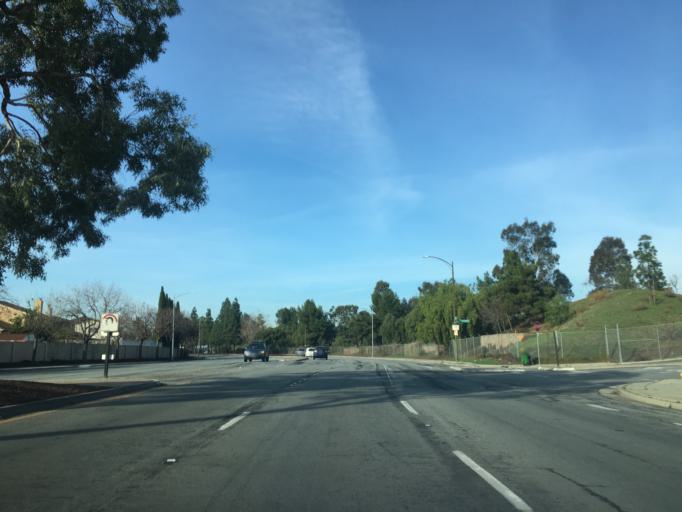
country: US
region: California
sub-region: Santa Clara County
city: Alum Rock
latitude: 37.3332
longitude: -121.8069
